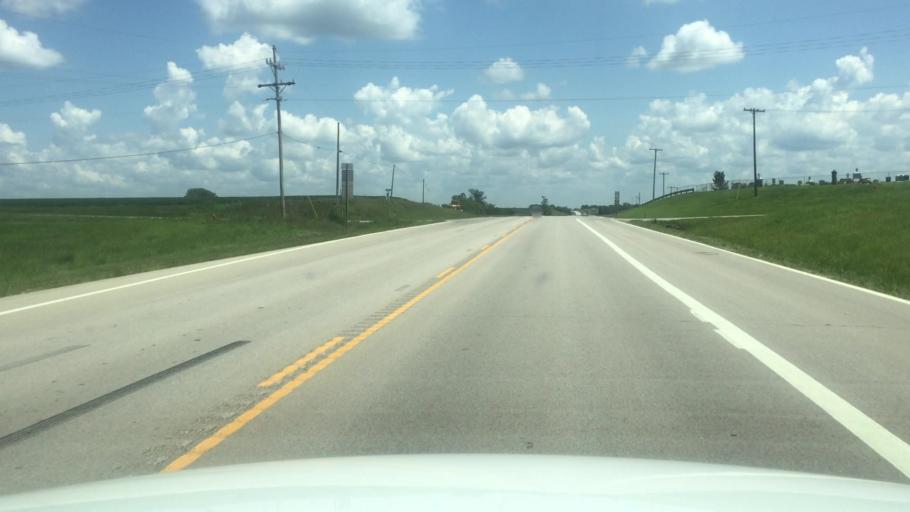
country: US
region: Kansas
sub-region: Brown County
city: Horton
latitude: 39.6675
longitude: -95.4907
